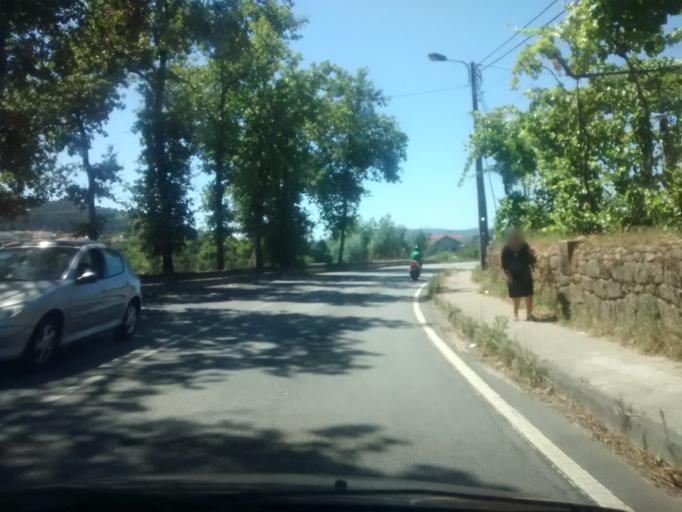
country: PT
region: Braga
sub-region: Braga
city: Oliveira
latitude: 41.5296
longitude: -8.4876
